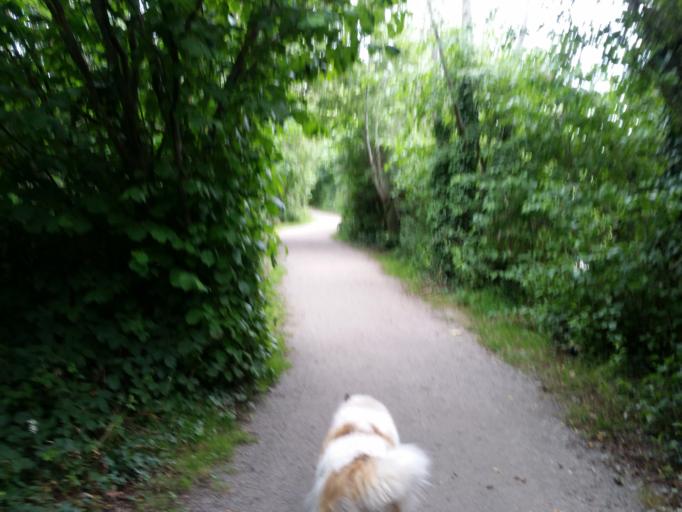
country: GB
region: Northern Ireland
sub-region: Castlereagh District
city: Castlereagh
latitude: 54.6084
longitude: -5.8838
